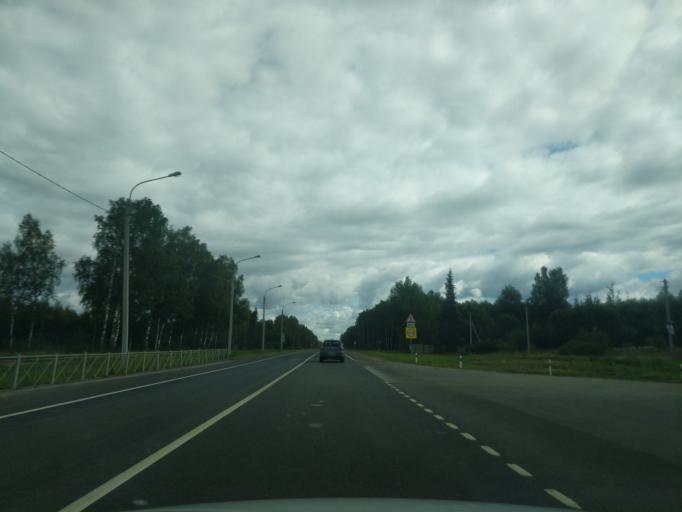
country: RU
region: Jaroslavl
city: Tunoshna
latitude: 57.5539
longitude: 40.1984
